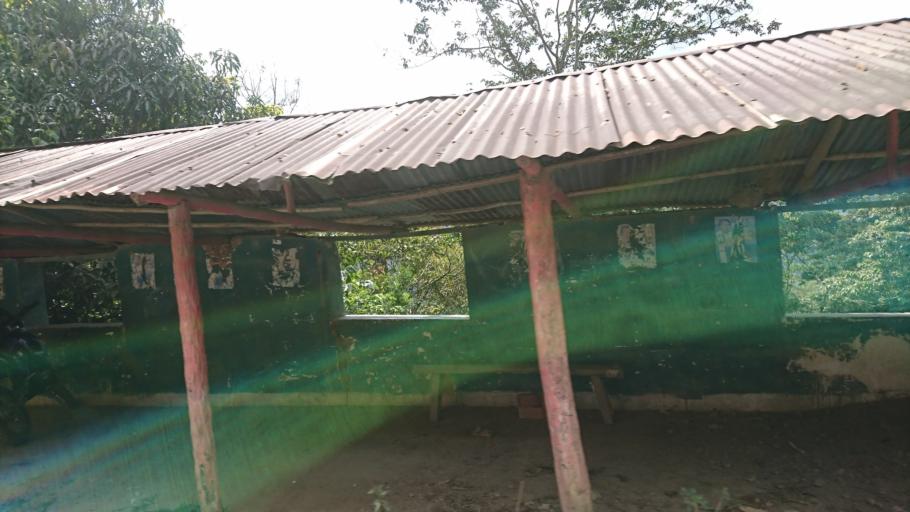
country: BO
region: La Paz
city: Coroico
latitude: -16.0880
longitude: -67.7856
